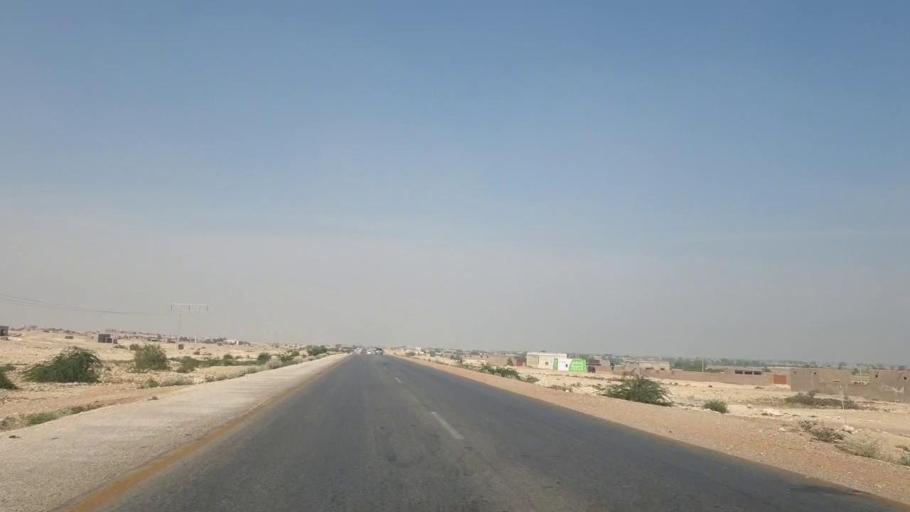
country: PK
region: Sindh
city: Hala
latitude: 25.7812
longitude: 68.2836
